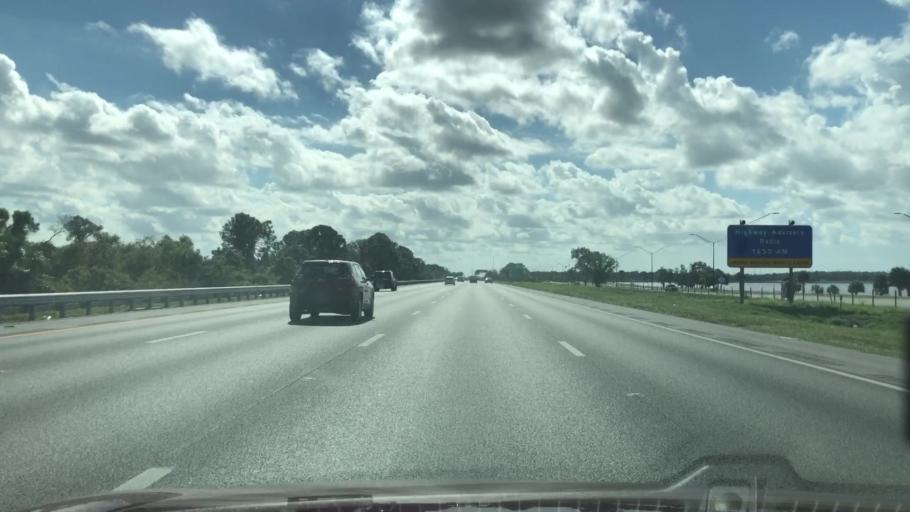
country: US
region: Florida
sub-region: Sarasota County
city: The Meadows
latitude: 27.3717
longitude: -82.4470
